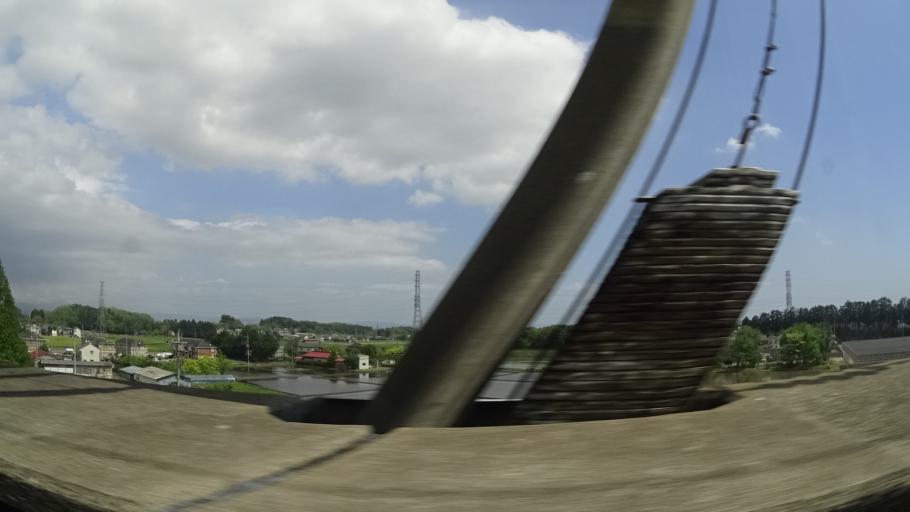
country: JP
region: Tochigi
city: Otawara
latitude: 36.8641
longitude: 139.9722
